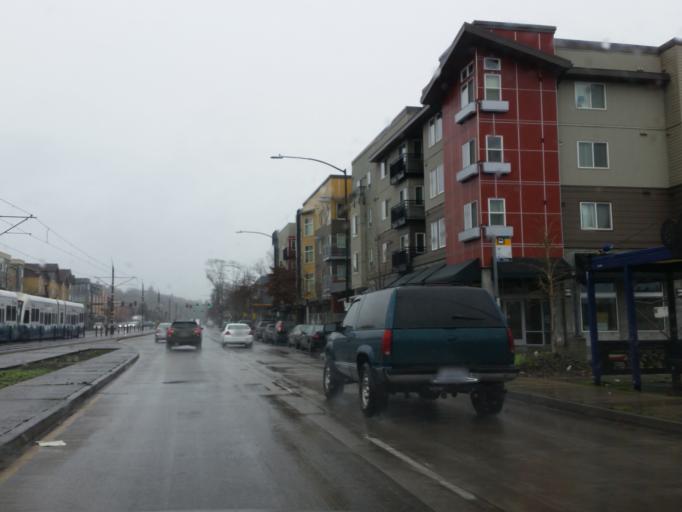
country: US
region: Washington
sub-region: King County
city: Seattle
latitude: 47.5611
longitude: -122.2934
